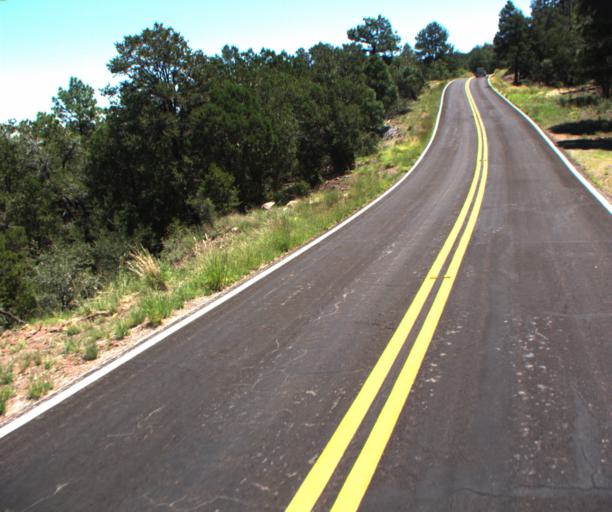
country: US
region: Arizona
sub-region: Greenlee County
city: Morenci
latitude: 33.4032
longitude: -109.3408
